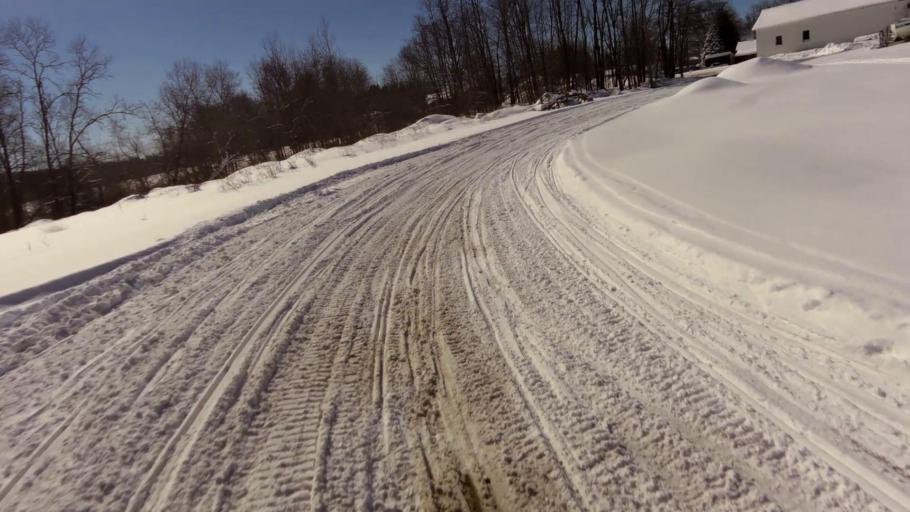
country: US
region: New York
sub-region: Chautauqua County
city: Mayville
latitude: 42.1641
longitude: -79.5838
